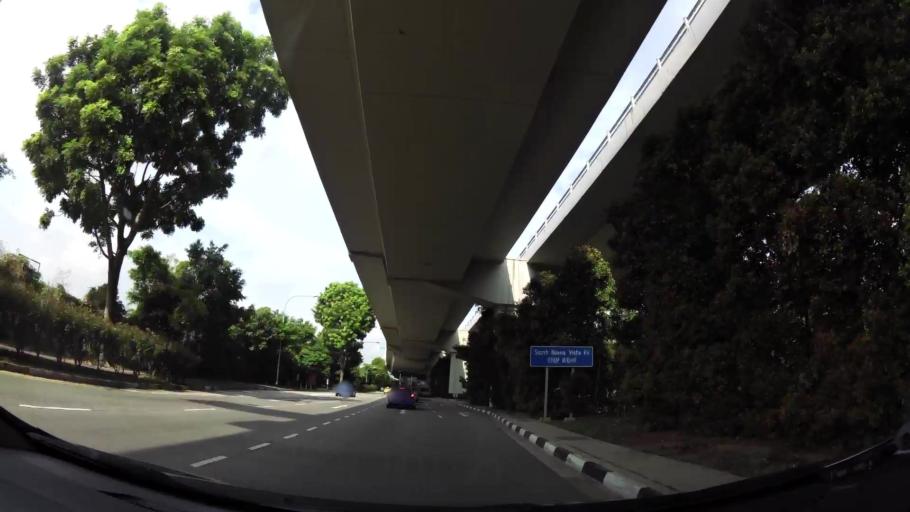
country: SG
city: Singapore
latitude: 1.2779
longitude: 103.7868
